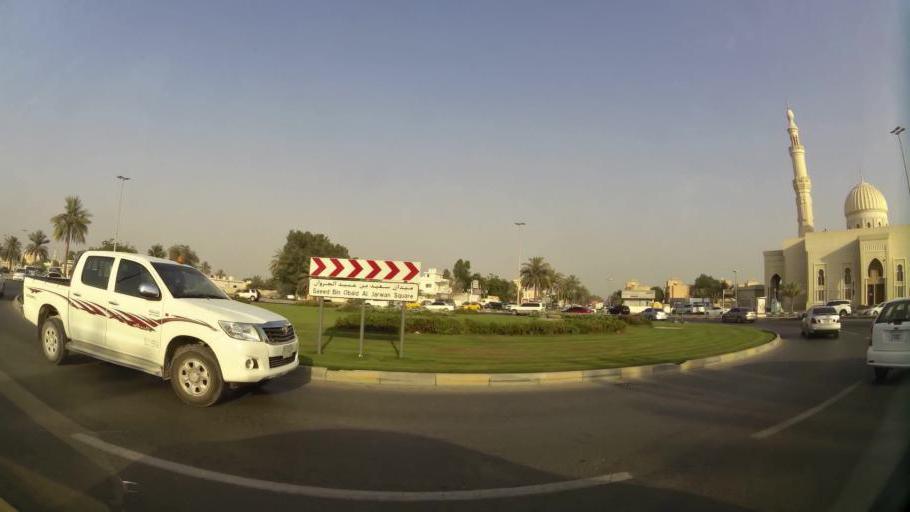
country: AE
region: Ash Shariqah
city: Sharjah
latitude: 25.3718
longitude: 55.4276
